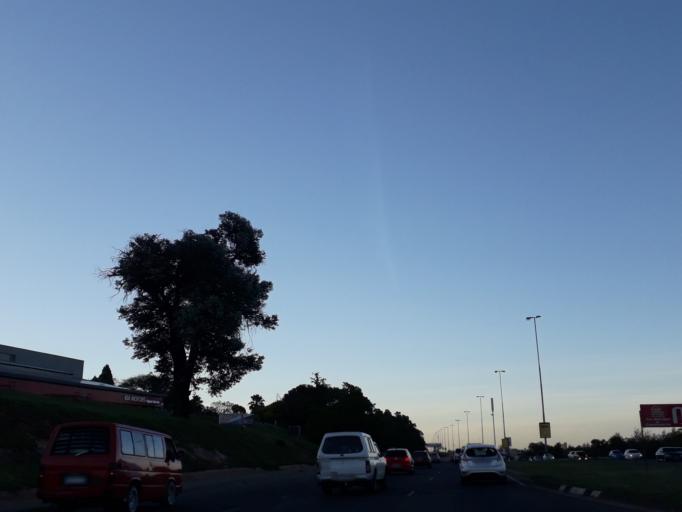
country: ZA
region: Gauteng
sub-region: City of Johannesburg Metropolitan Municipality
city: Roodepoort
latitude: -26.1446
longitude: 27.9216
